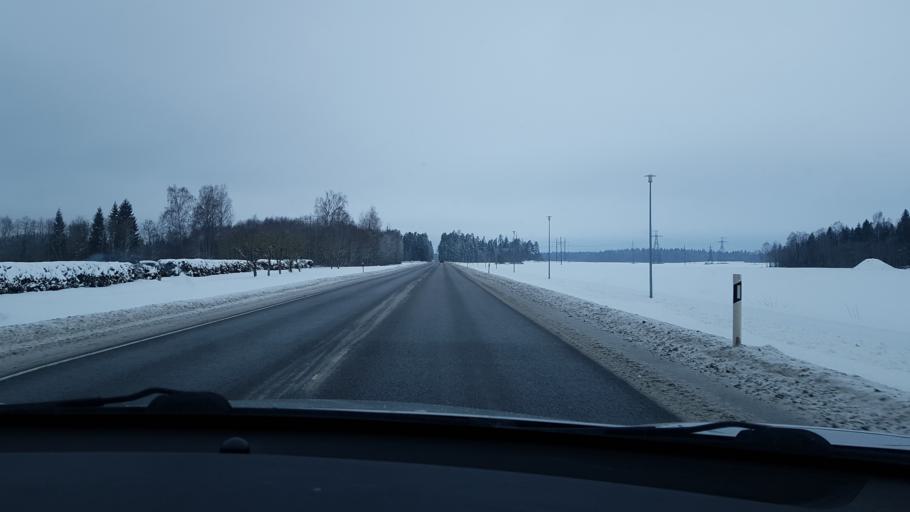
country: EE
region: Jaervamaa
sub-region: Paide linn
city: Paide
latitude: 58.8753
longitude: 25.5020
